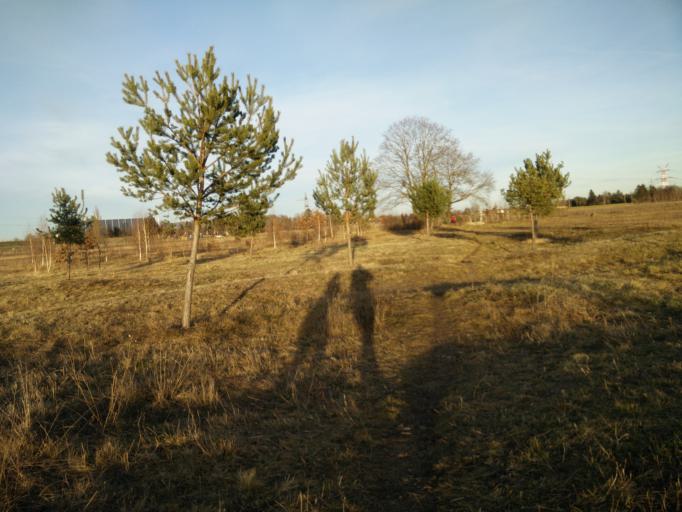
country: DE
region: Bavaria
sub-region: Upper Bavaria
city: Pasing
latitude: 48.1708
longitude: 11.4272
